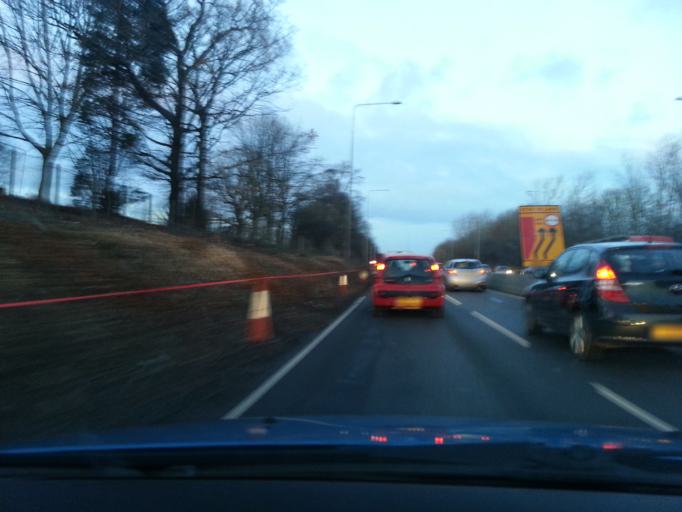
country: GB
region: England
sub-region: Gateshead
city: Lamesley
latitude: 54.9345
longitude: -1.6284
